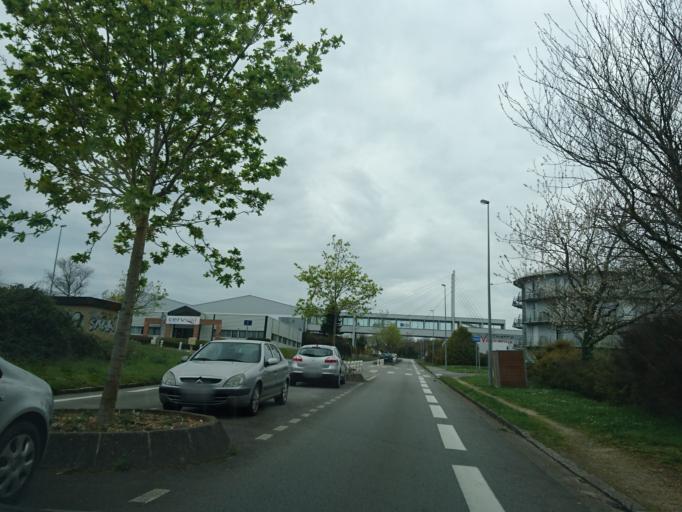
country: FR
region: Brittany
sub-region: Departement du Finistere
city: Roscanvel
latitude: 48.3625
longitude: -4.5660
